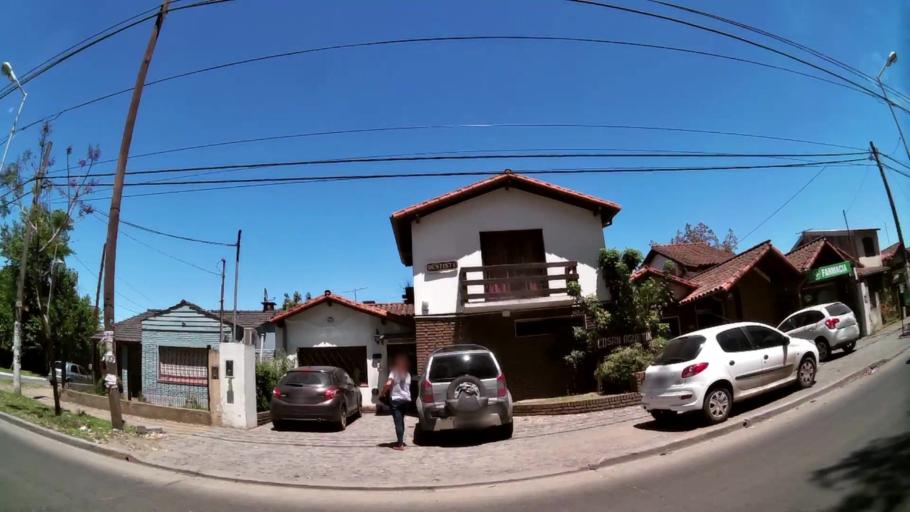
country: AR
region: Buenos Aires
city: Hurlingham
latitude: -34.5142
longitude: -58.7072
